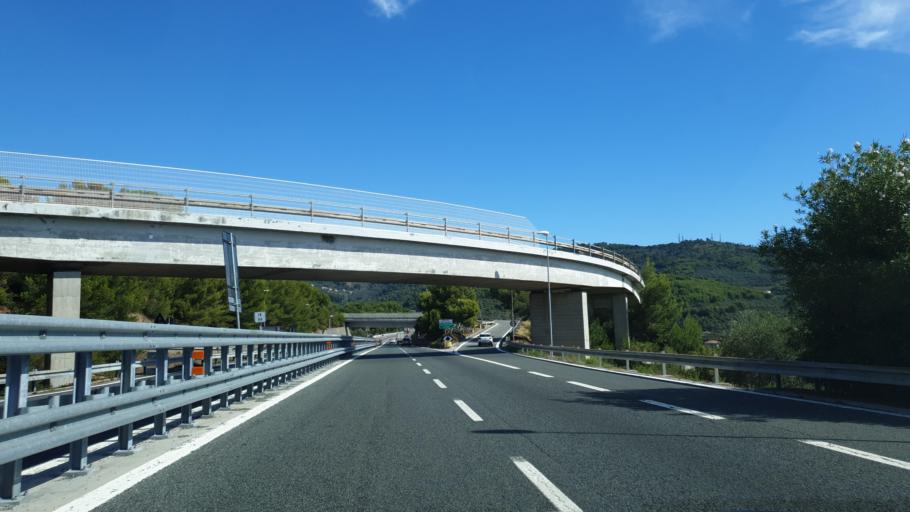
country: IT
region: Liguria
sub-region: Provincia di Imperia
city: San Bartolomeo al Mare
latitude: 43.9271
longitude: 8.0966
